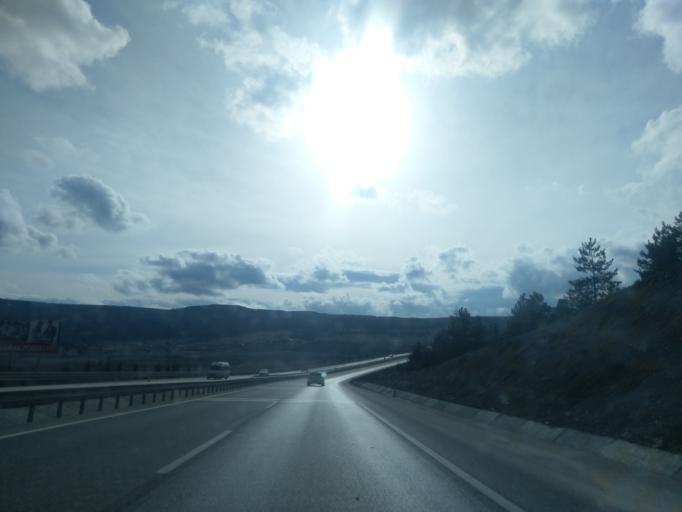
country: TR
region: Kuetahya
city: Sabuncu
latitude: 39.5748
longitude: 30.1177
